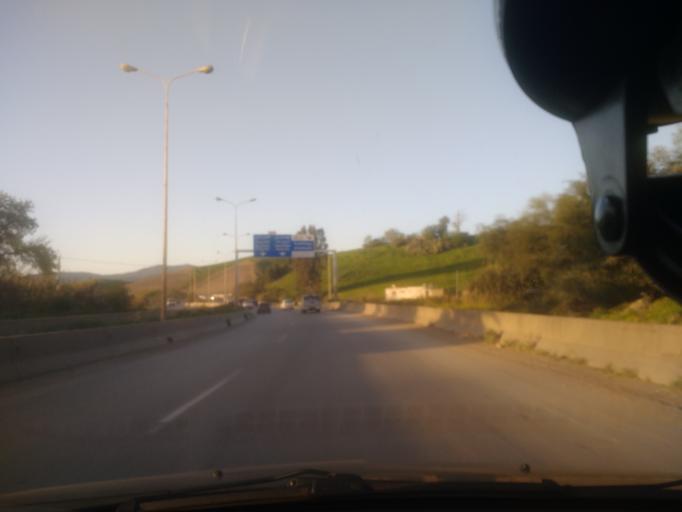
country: DZ
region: Tizi Ouzou
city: Tizi Ouzou
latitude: 36.7142
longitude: 4.0026
